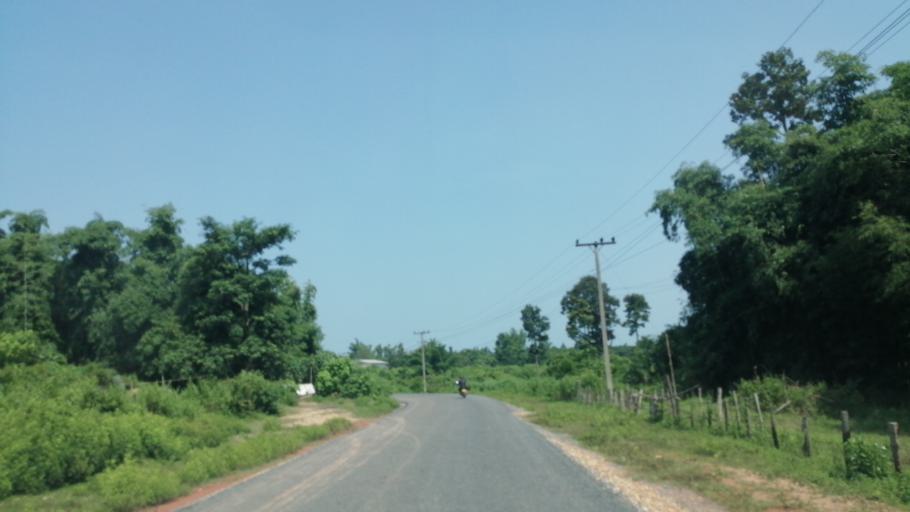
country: LA
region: Bolikhamxai
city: Bolikhan
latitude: 18.4596
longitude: 103.7982
